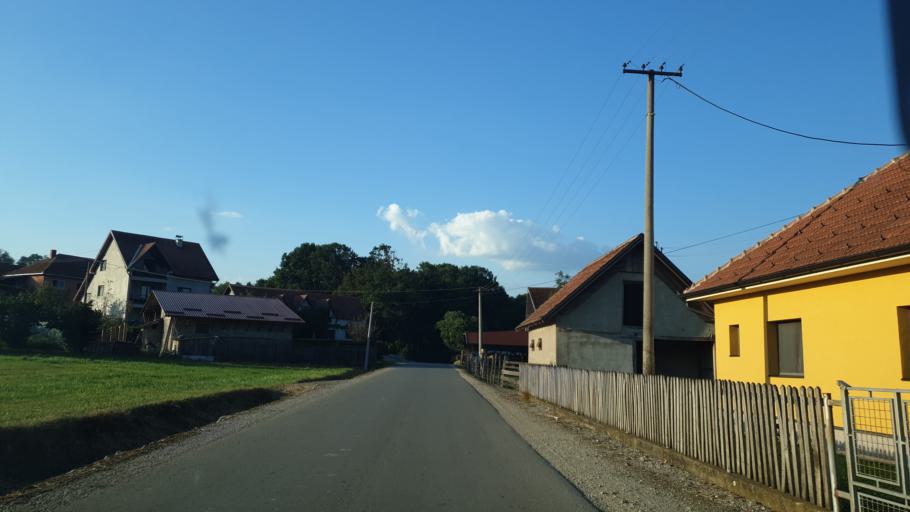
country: RS
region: Central Serbia
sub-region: Zlatiborski Okrug
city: Pozega
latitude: 43.8709
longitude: 19.9913
